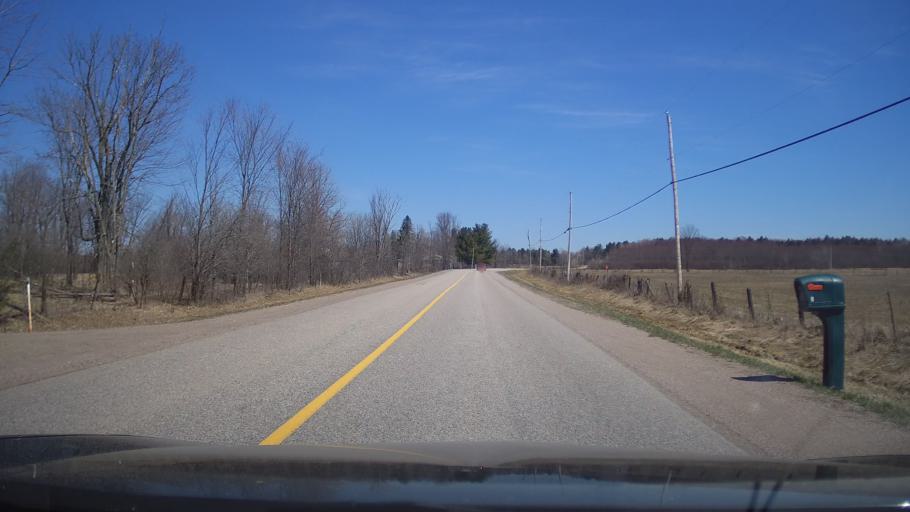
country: CA
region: Ontario
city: Arnprior
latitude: 45.5366
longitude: -76.3692
